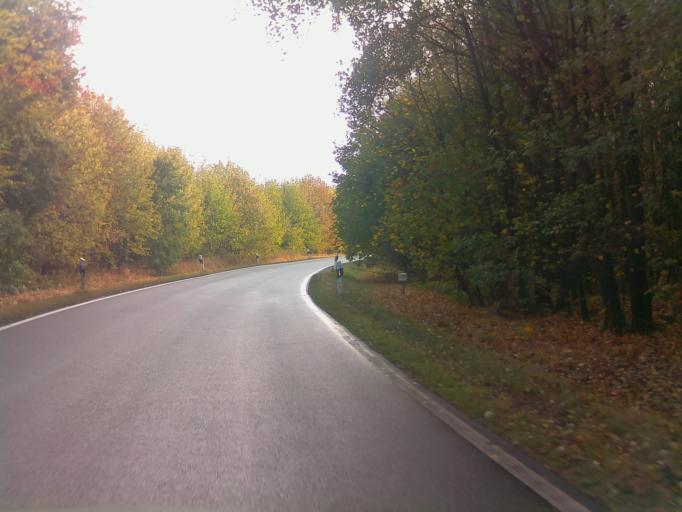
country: DE
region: Hesse
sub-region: Regierungsbezirk Giessen
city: Freiensteinau
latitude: 50.4754
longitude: 9.4264
